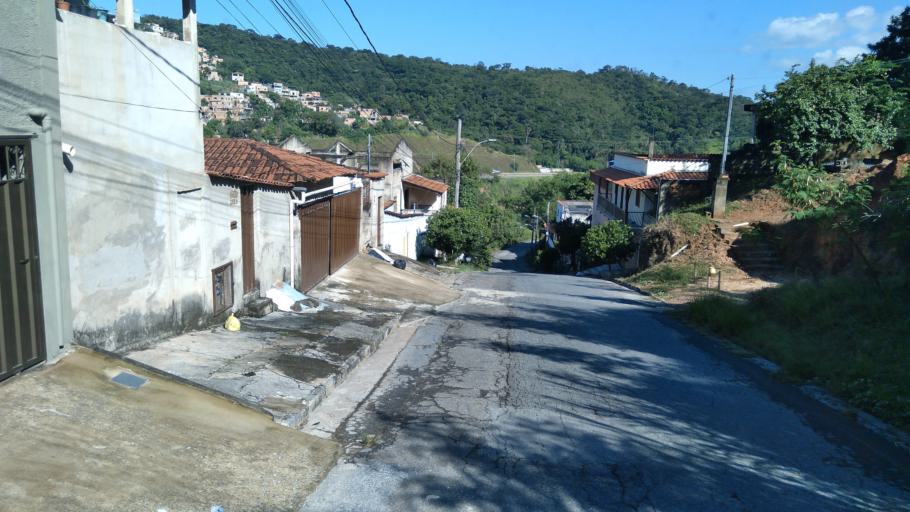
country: BR
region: Minas Gerais
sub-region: Santa Luzia
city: Santa Luzia
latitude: -19.8288
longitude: -43.9019
